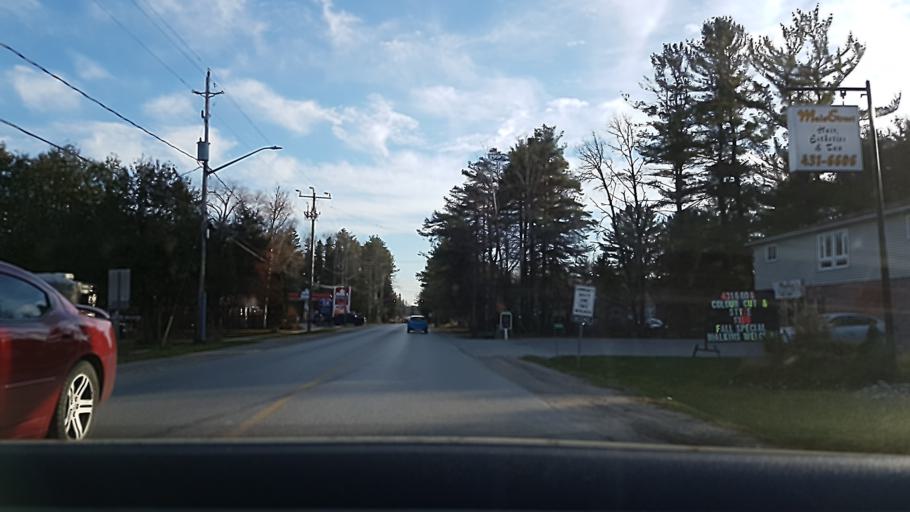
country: CA
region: Ontario
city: Keswick
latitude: 44.3294
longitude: -79.5431
